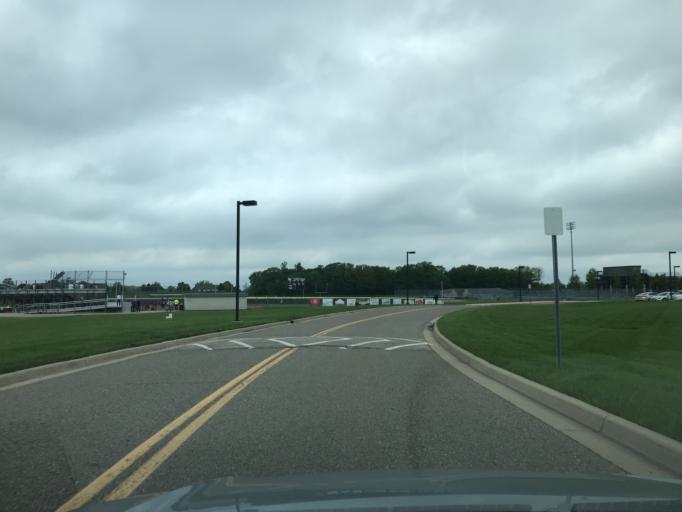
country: US
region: Michigan
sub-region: Oakland County
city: Wixom
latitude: 42.4658
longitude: -83.5692
